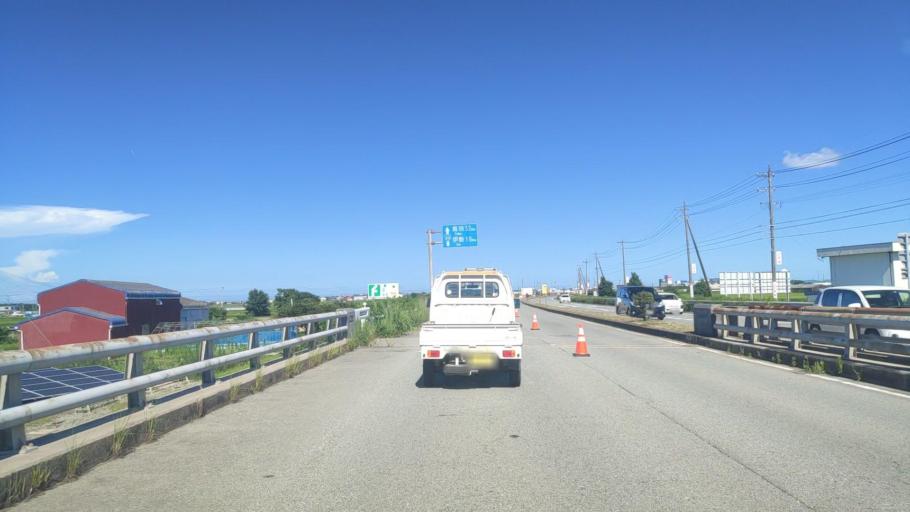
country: JP
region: Mie
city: Ise
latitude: 34.5873
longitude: 136.5963
